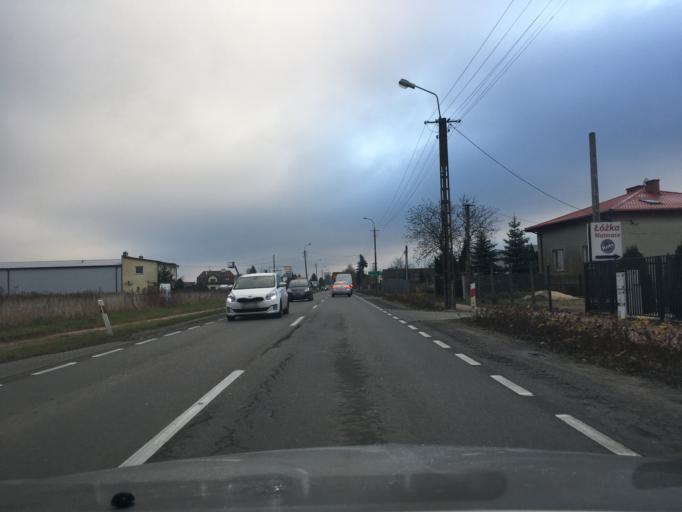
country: PL
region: Masovian Voivodeship
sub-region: Powiat piaseczynski
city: Lesznowola
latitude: 52.0850
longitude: 20.9526
